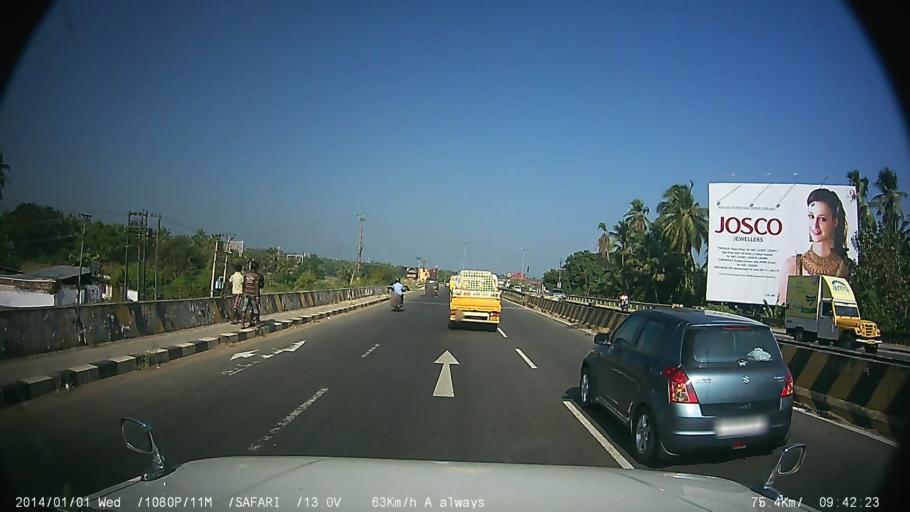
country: IN
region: Kerala
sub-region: Thrissur District
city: Trichur
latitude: 10.4389
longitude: 76.2639
